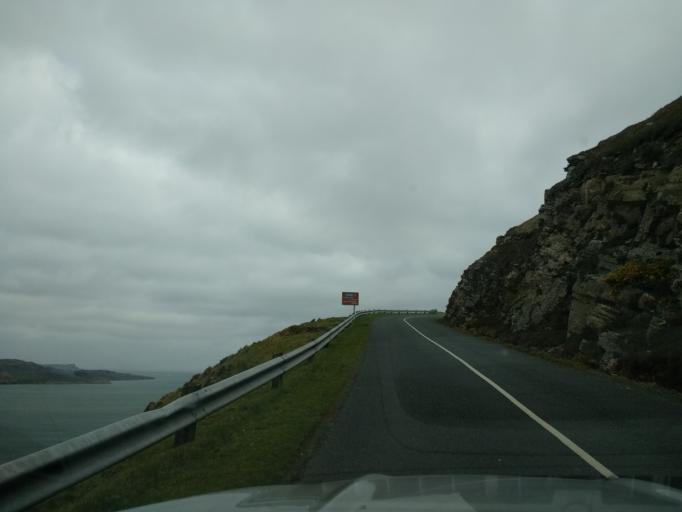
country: IE
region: Ulster
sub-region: County Donegal
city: Buncrana
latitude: 55.1833
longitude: -7.5959
